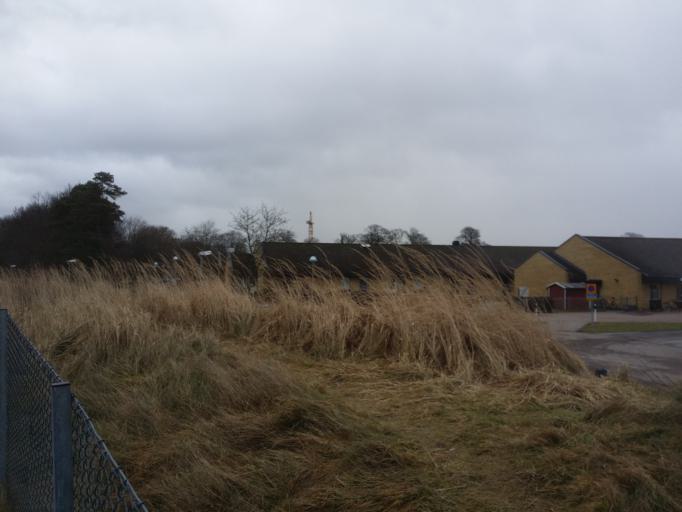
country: SE
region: Skane
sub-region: Angelholms Kommun
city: AEngelholm
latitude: 56.2396
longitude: 12.8518
